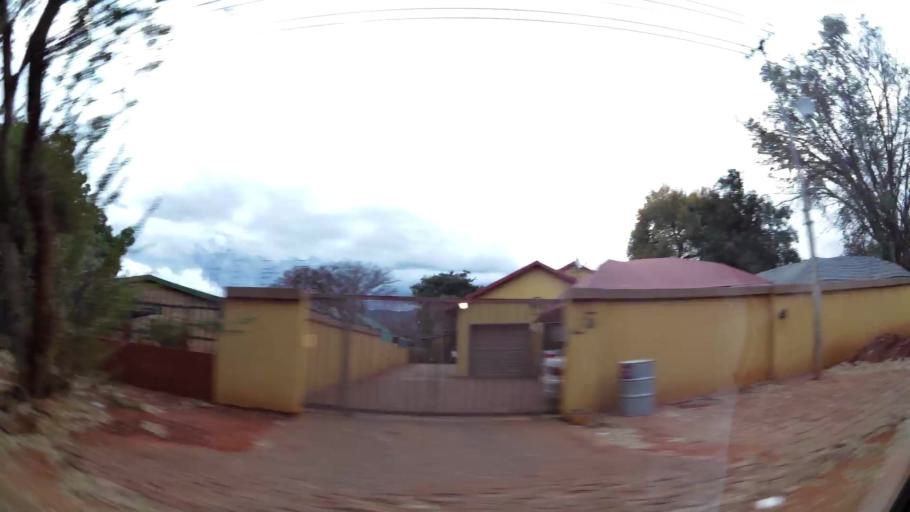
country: ZA
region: Limpopo
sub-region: Waterberg District Municipality
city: Mokopane
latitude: -24.1949
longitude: 28.9902
